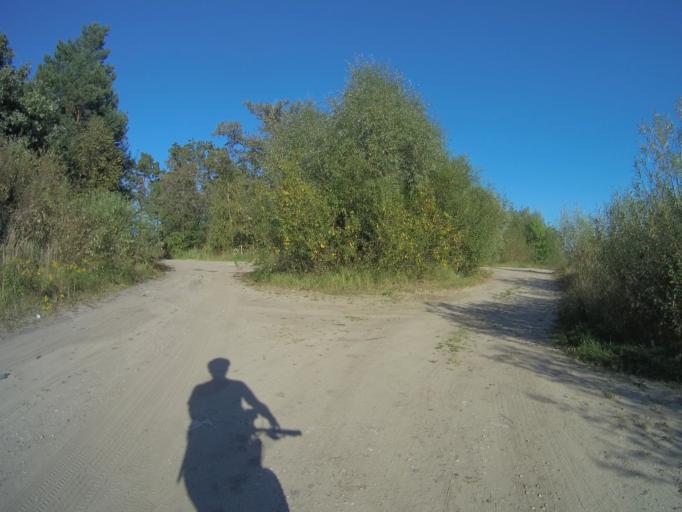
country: RU
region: Vladimir
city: Kommunar
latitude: 56.0515
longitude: 40.4201
